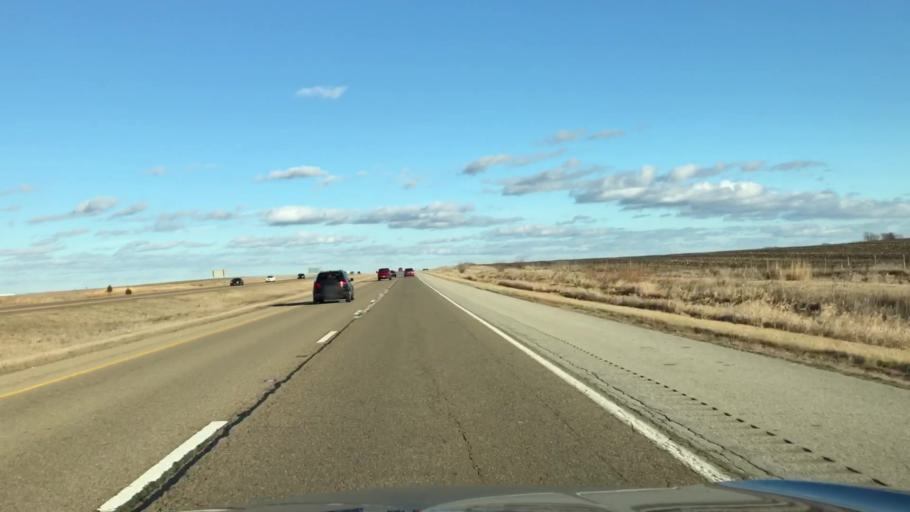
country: US
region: Illinois
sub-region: McLean County
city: Lexington
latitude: 40.6575
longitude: -88.7923
